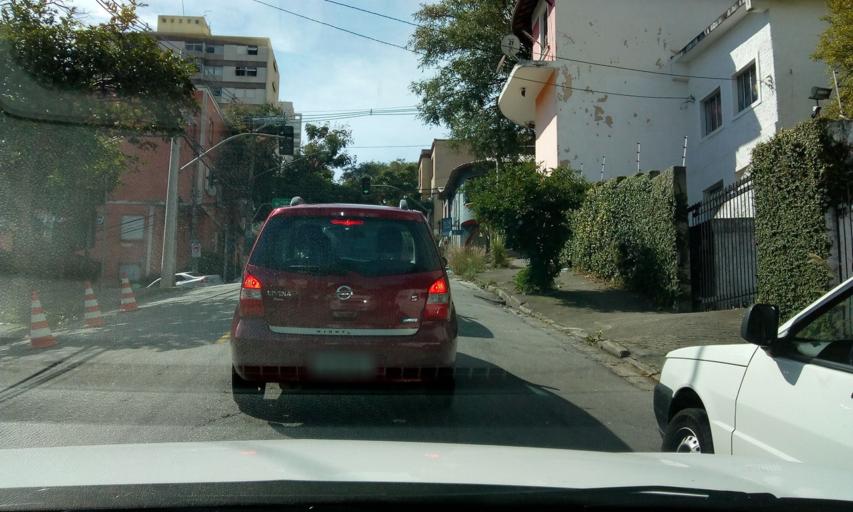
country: BR
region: Sao Paulo
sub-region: Sao Paulo
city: Sao Paulo
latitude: -23.5410
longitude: -46.6744
